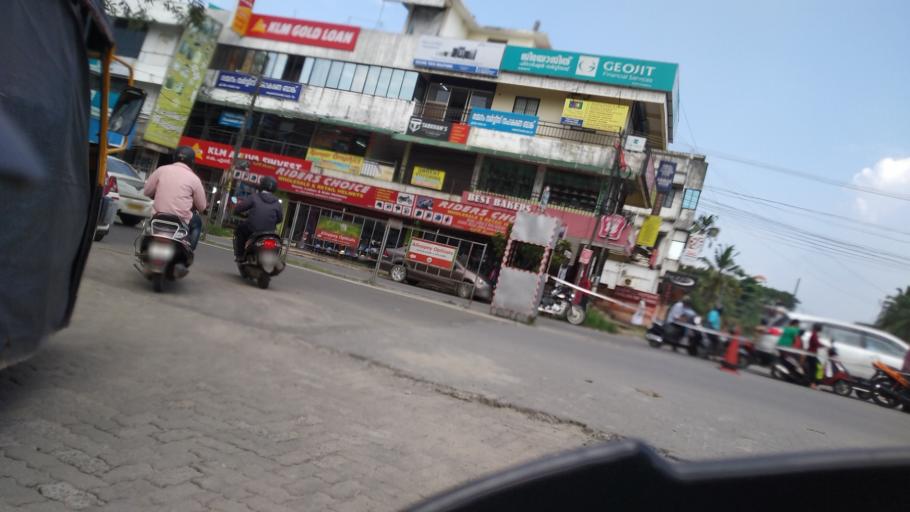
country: IN
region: Kerala
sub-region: Ernakulam
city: Cochin
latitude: 9.9835
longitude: 76.2957
